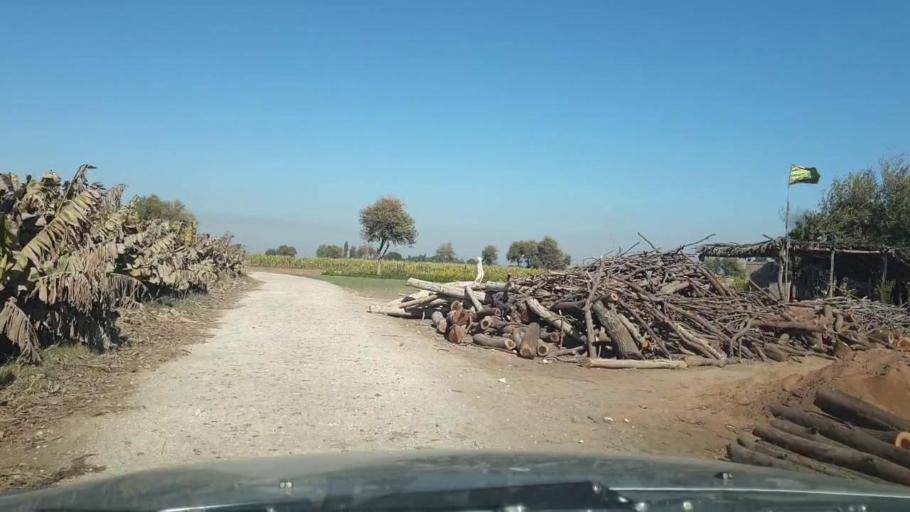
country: PK
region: Sindh
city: Ghotki
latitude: 28.0477
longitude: 69.2419
